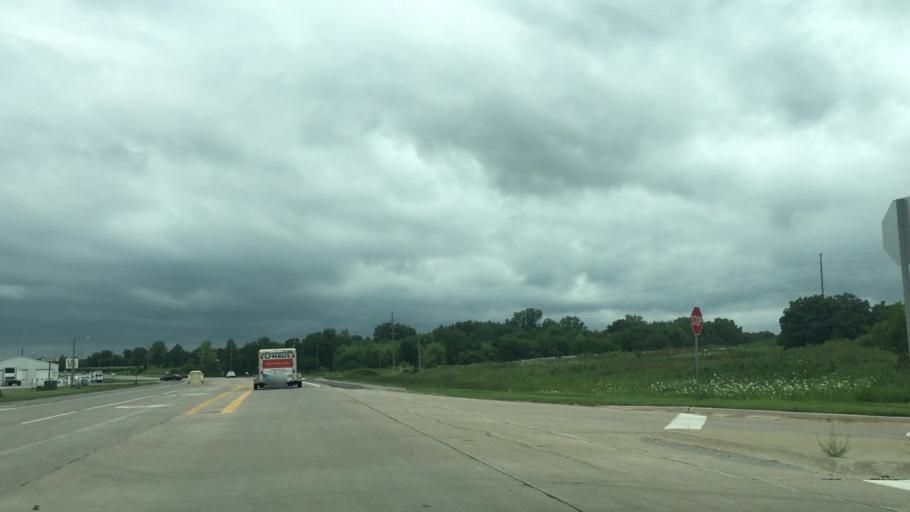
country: US
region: Iowa
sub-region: Johnson County
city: Tiffin
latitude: 41.6993
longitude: -91.6274
